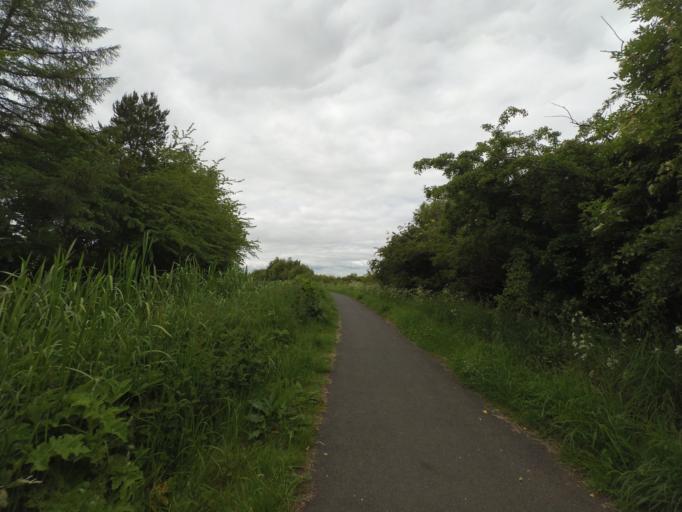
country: GB
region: Scotland
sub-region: West Lothian
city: Linlithgow
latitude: 55.9676
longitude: -3.6172
